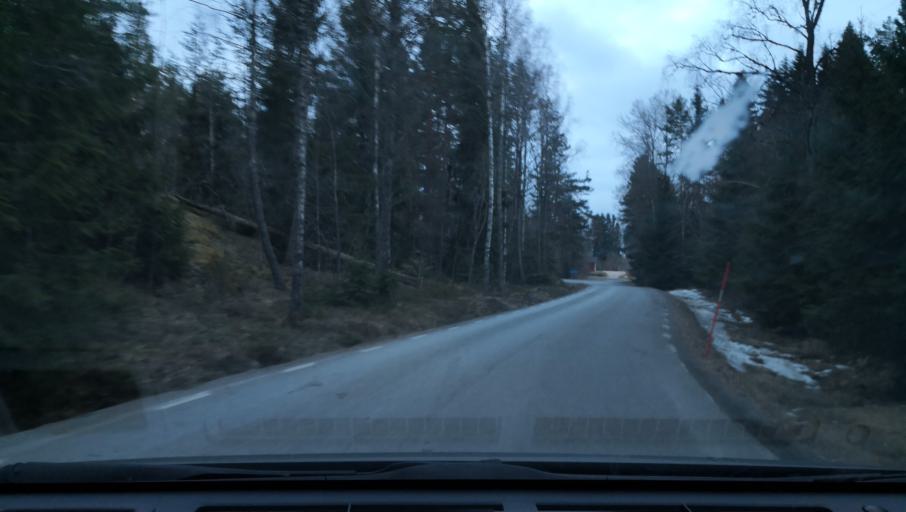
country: SE
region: Vaestmanland
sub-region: Kopings Kommun
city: Kolsva
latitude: 59.5678
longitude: 15.7796
